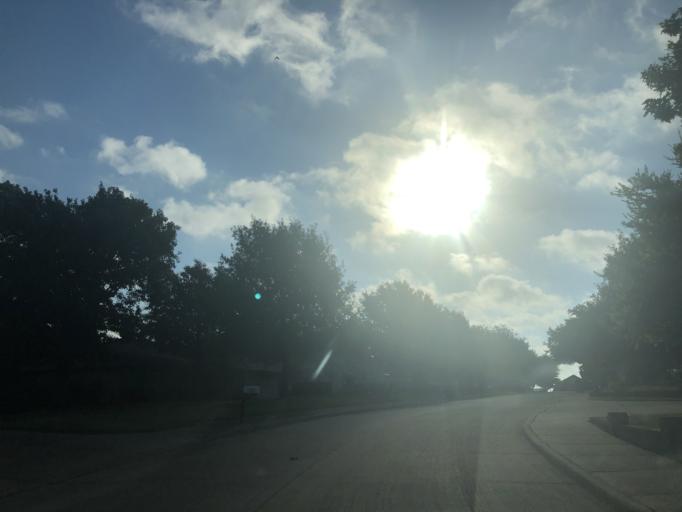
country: US
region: Texas
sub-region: Dallas County
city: Duncanville
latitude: 32.6709
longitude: -96.9124
